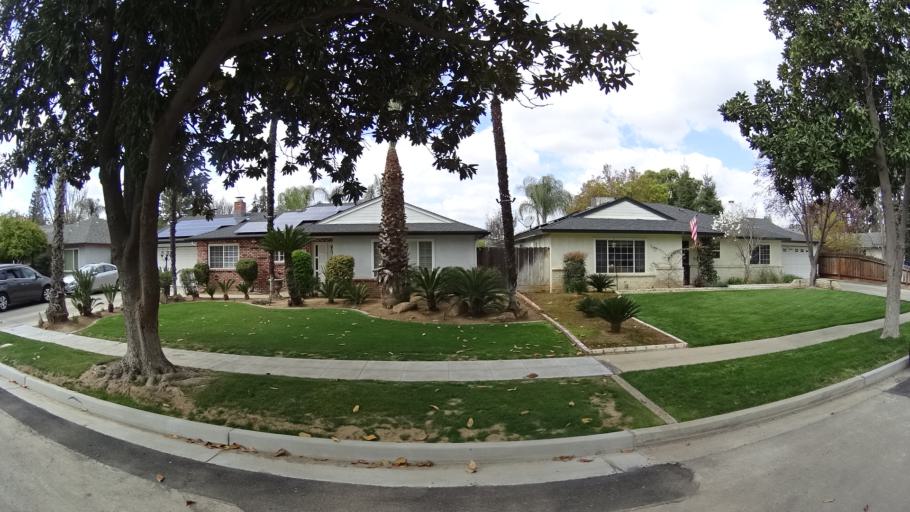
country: US
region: California
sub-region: Fresno County
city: Fresno
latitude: 36.8170
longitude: -119.8496
